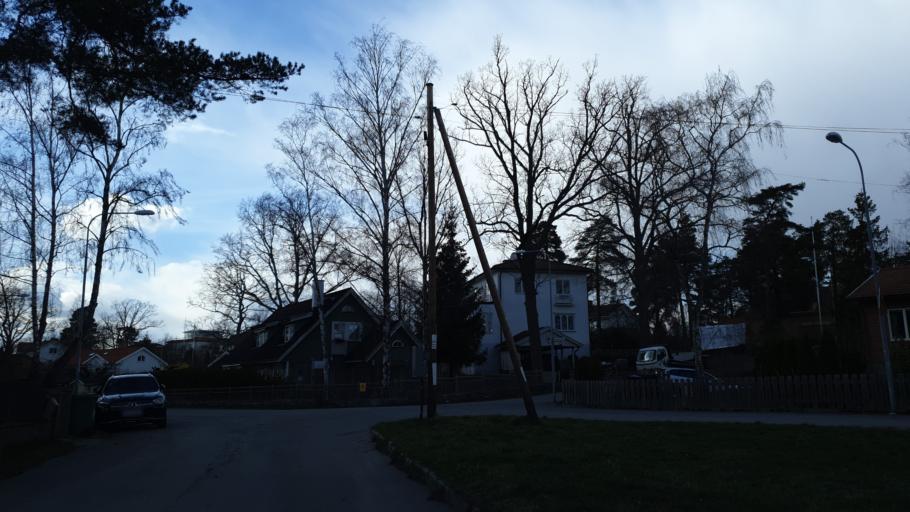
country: SE
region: Stockholm
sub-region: Lidingo
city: Lidingoe
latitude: 59.3715
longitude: 18.1208
